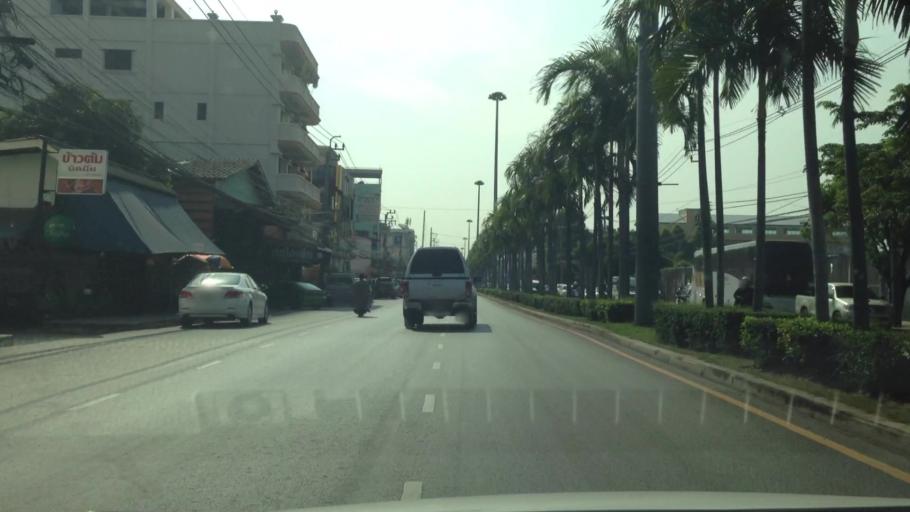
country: TH
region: Samut Prakan
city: Samut Prakan
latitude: 13.5865
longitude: 100.5991
